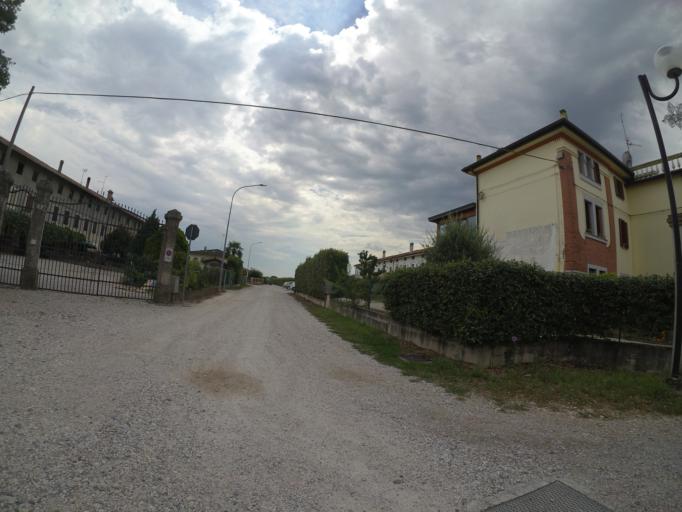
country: IT
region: Friuli Venezia Giulia
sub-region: Provincia di Udine
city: Bertiolo
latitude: 45.9432
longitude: 13.0550
